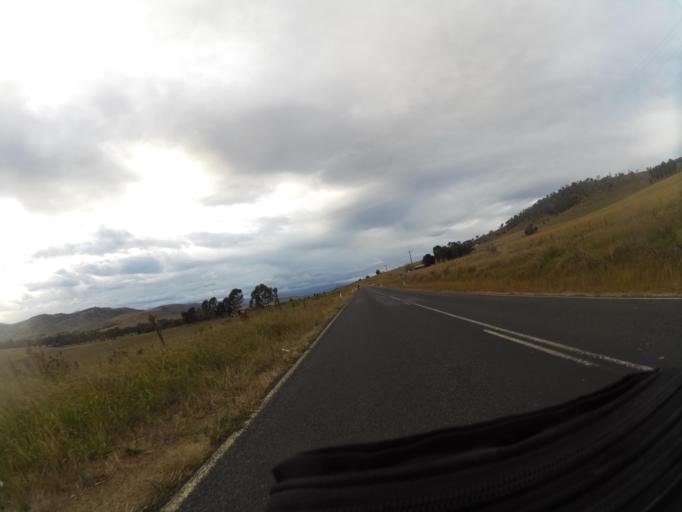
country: AU
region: New South Wales
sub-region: Snowy River
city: Jindabyne
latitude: -36.0768
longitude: 147.9723
